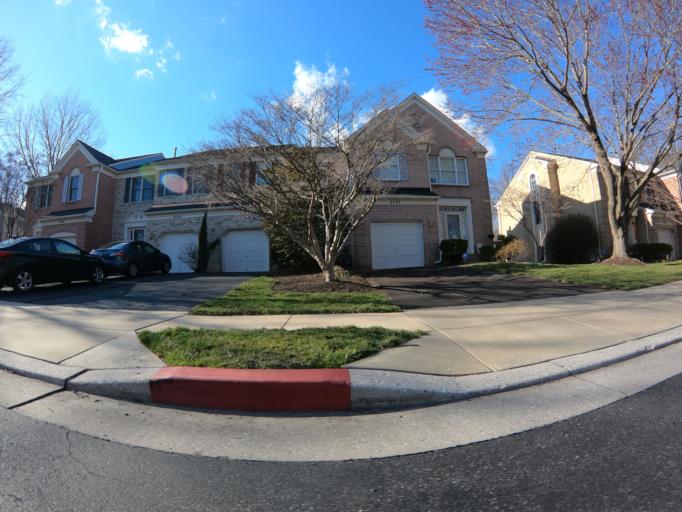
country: US
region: Maryland
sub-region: Howard County
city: Ellicott City
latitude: 39.2580
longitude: -76.8005
